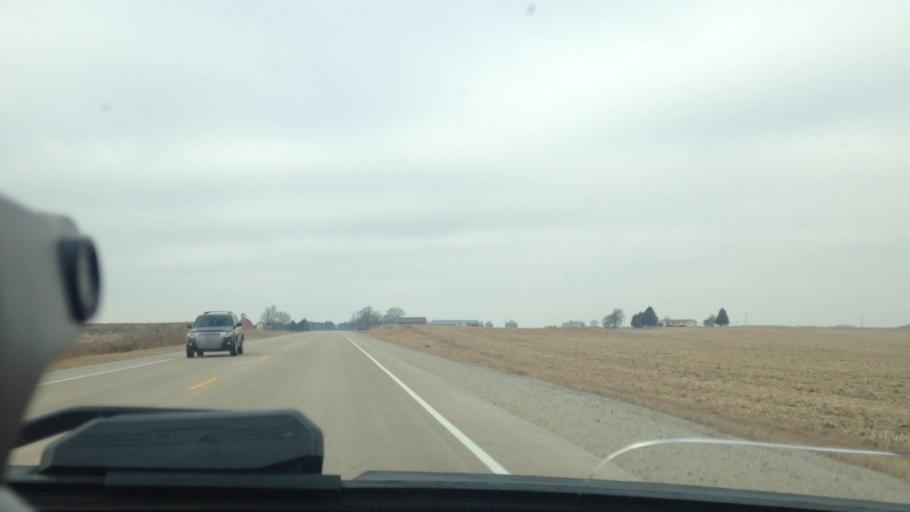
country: US
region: Wisconsin
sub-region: Dodge County
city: Juneau
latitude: 43.4735
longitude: -88.7368
